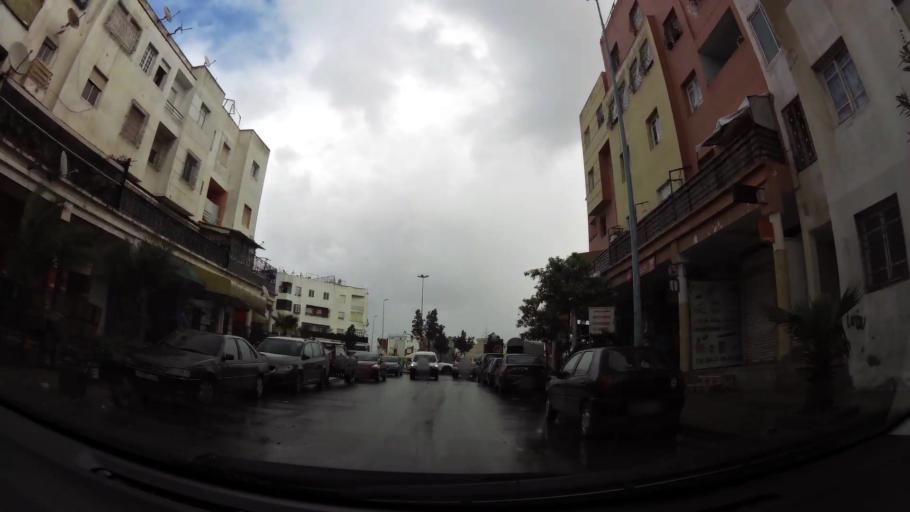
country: MA
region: Grand Casablanca
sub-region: Casablanca
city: Casablanca
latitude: 33.5454
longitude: -7.6738
